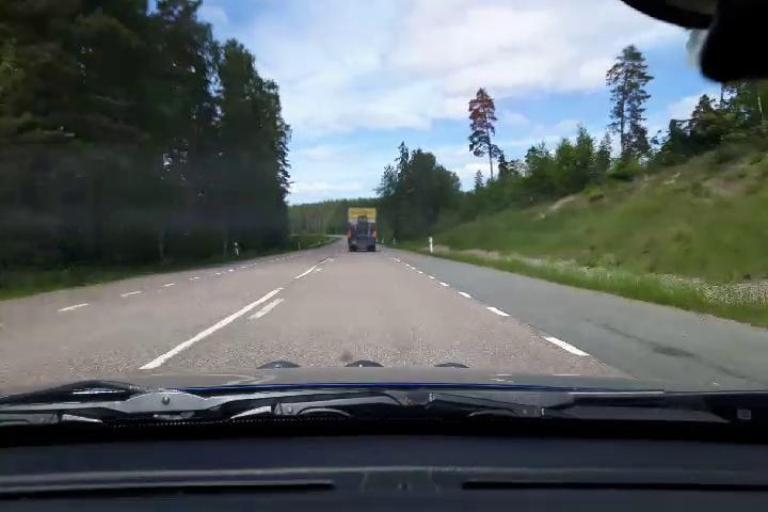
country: SE
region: Uppsala
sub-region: Osthammars Kommun
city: Bjorklinge
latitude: 60.0966
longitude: 17.5538
